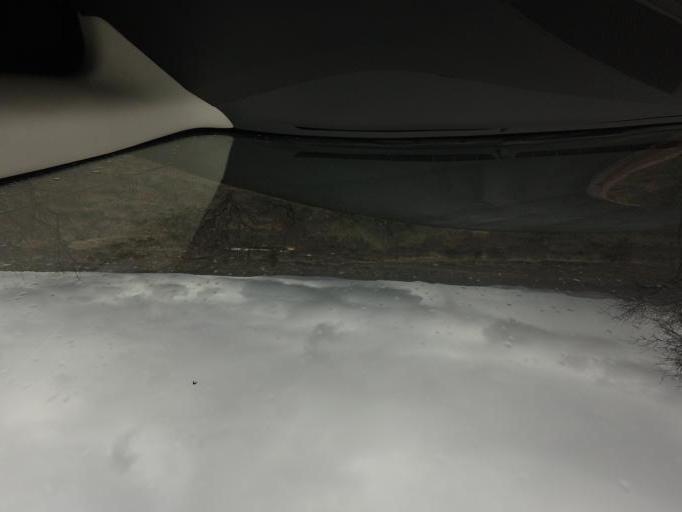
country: US
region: Arizona
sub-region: Yavapai County
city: Clarkdale
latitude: 34.7707
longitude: -112.0265
